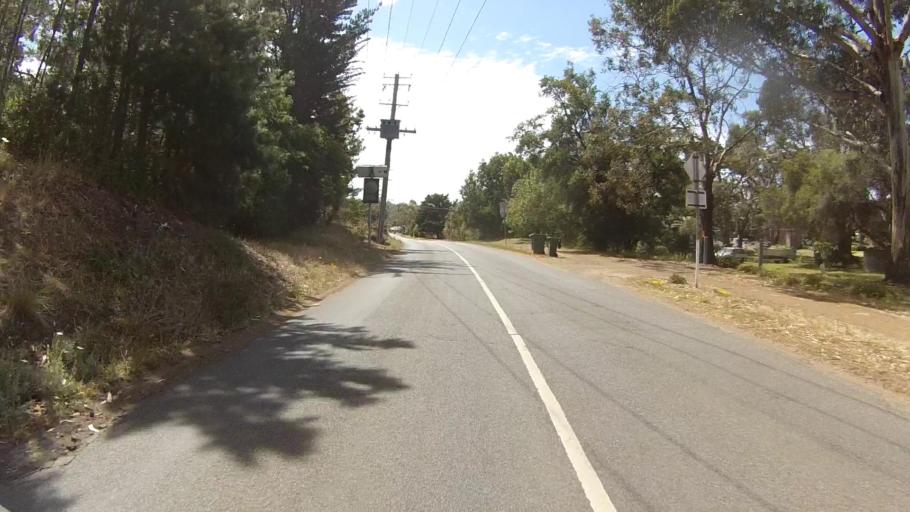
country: AU
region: Tasmania
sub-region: Kingborough
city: Blackmans Bay
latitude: -43.0274
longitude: 147.4166
